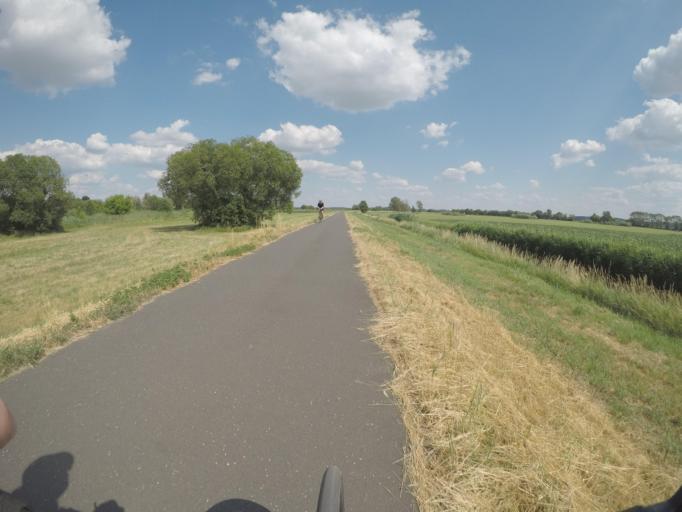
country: DE
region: Brandenburg
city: Ketzin
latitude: 52.4600
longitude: 12.8603
